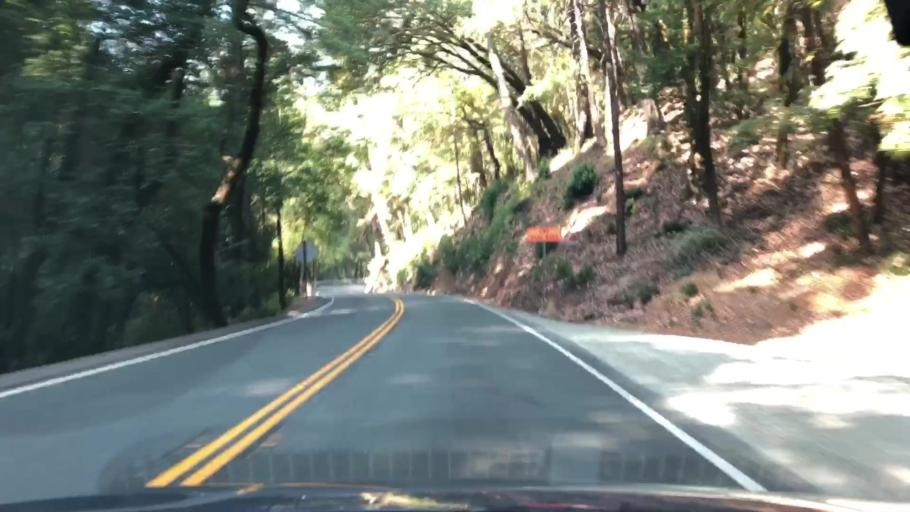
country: US
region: California
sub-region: Napa County
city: Calistoga
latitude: 38.6668
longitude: -122.5901
